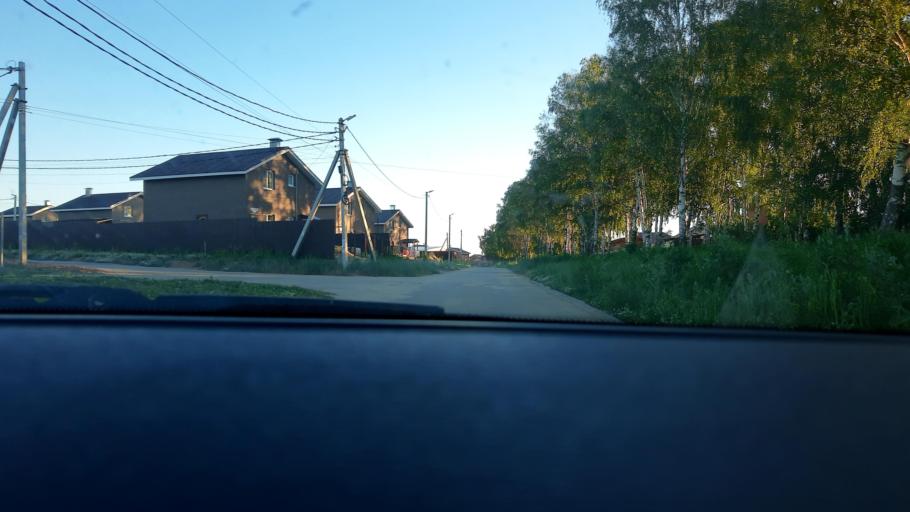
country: RU
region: Nizjnij Novgorod
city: Afonino
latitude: 56.1951
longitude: 44.0810
